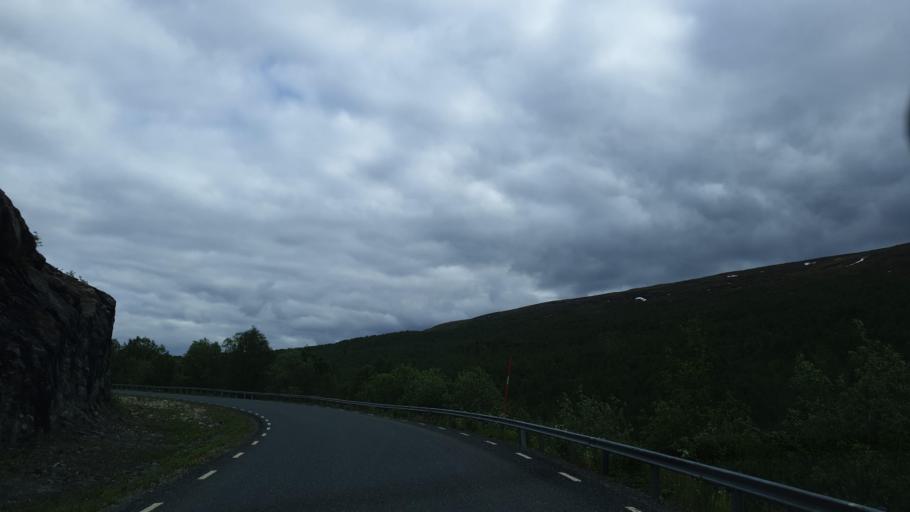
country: NO
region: Nordland
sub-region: Hattfjelldal
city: Hattfjelldal
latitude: 65.4236
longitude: 14.6064
